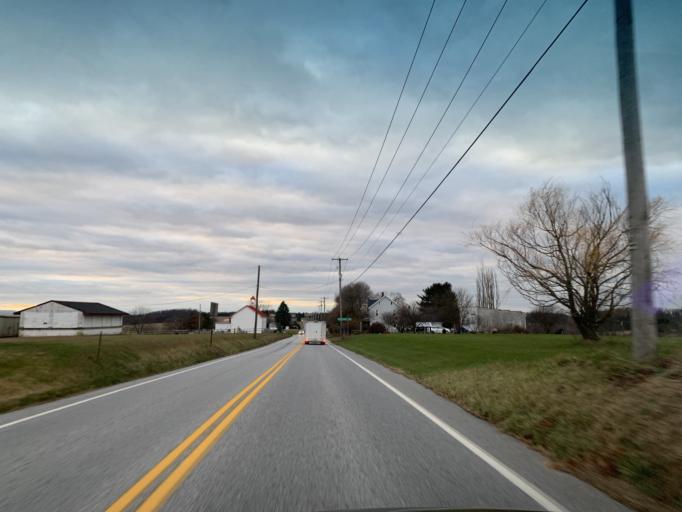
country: US
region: Pennsylvania
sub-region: York County
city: Shrewsbury
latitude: 39.7828
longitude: -76.6377
